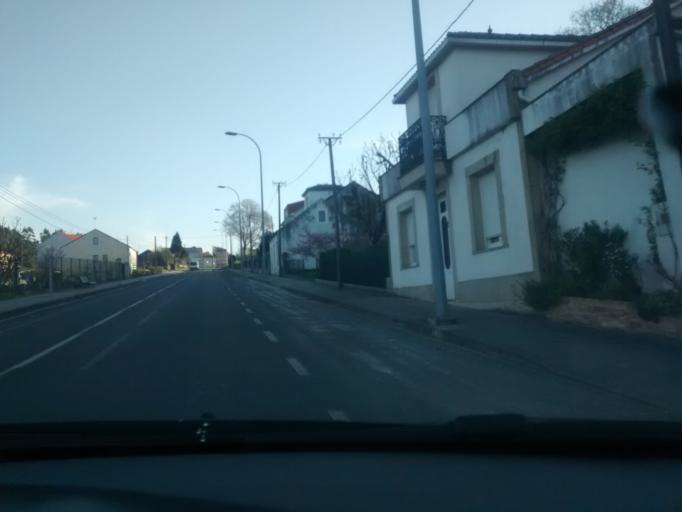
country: ES
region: Galicia
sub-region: Provincia de Pontevedra
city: A Estrada
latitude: 42.6957
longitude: -8.4832
